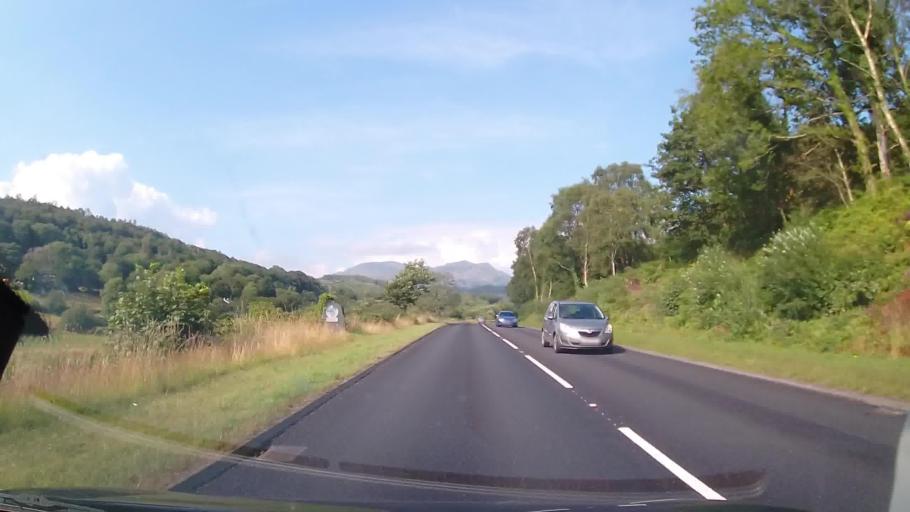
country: GB
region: Wales
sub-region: Gwynedd
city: Penrhyndeudraeth
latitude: 52.9343
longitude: -4.0592
